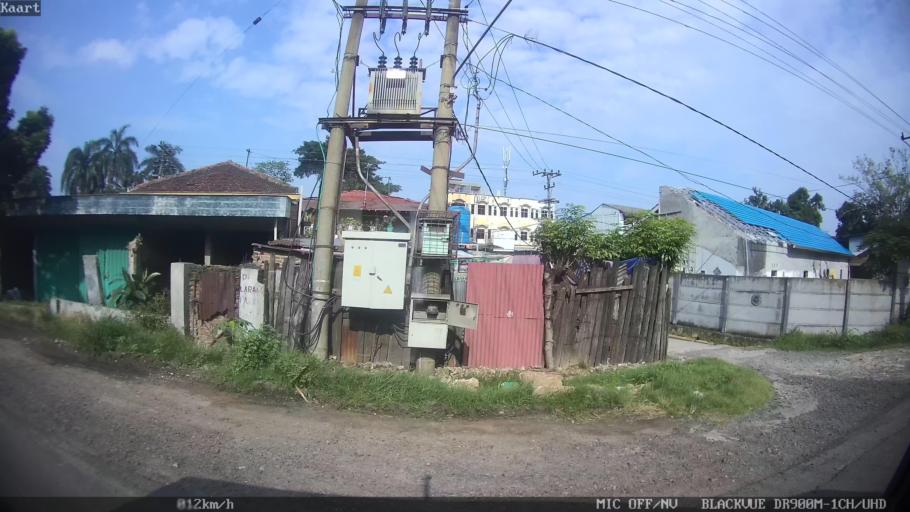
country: ID
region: Lampung
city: Panjang
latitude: -5.4814
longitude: 105.3259
